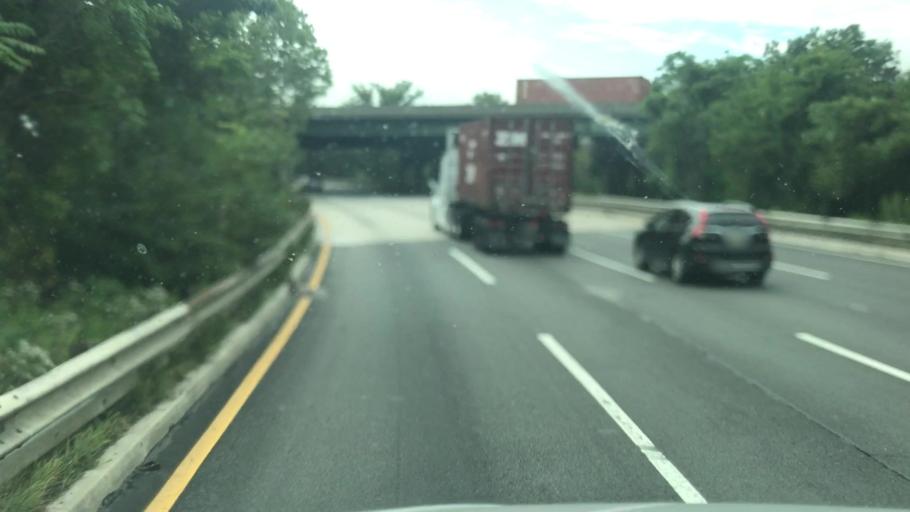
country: US
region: New Jersey
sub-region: Bergen County
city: Ridgefield Park
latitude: 40.8647
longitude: -74.0113
